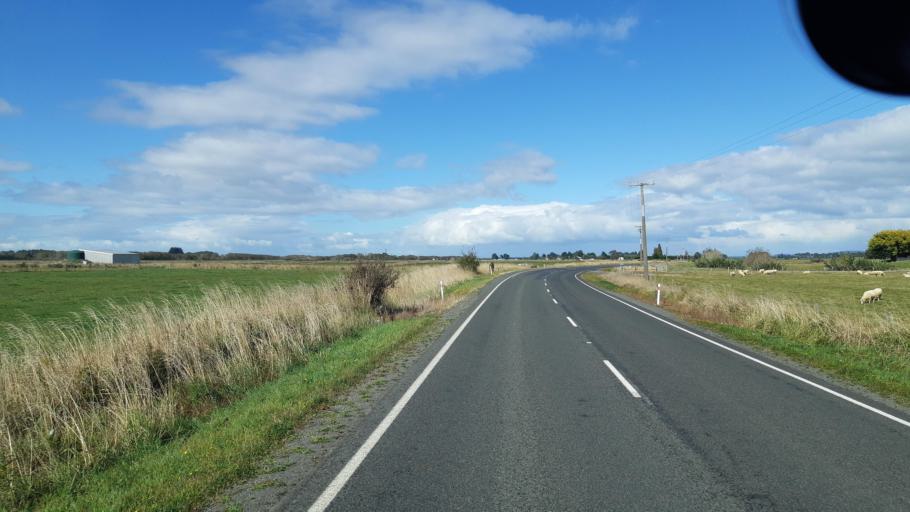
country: NZ
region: Southland
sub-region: Southland District
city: Winton
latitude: -45.9871
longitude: 168.1106
